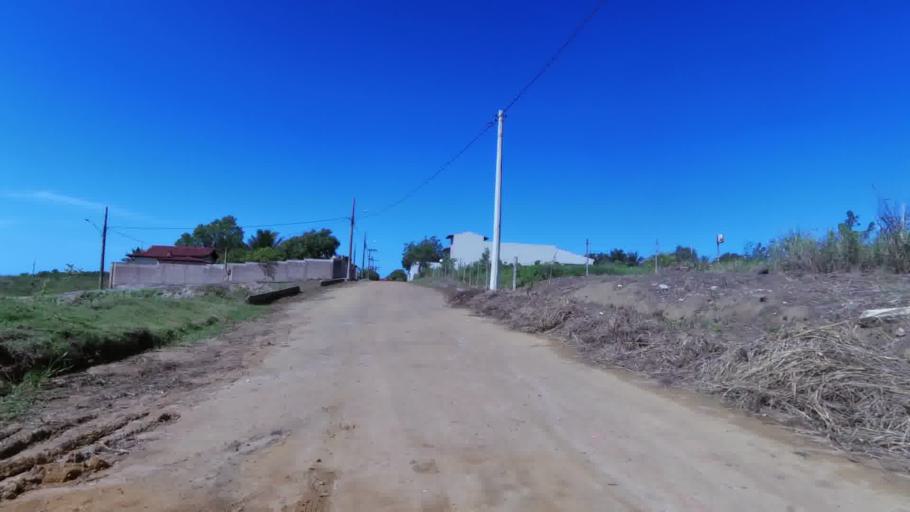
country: BR
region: Espirito Santo
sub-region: Piuma
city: Piuma
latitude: -20.8010
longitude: -40.5985
